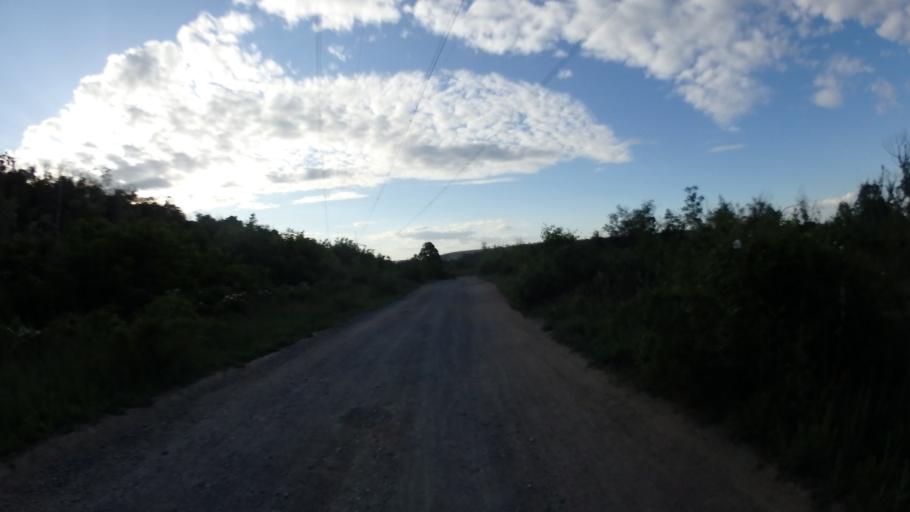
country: CZ
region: South Moravian
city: Ostopovice
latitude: 49.1543
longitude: 16.5446
